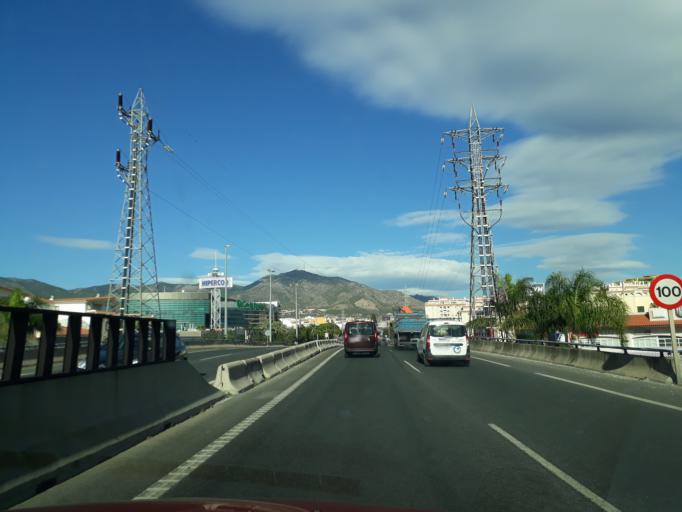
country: ES
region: Andalusia
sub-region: Provincia de Malaga
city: Fuengirola
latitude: 36.5454
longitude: -4.6331
